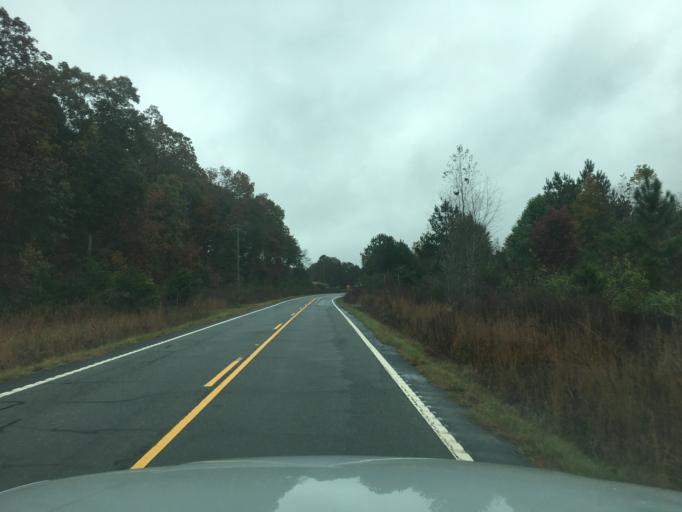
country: US
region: South Carolina
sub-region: Pickens County
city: Liberty
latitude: 34.7537
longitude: -82.7199
